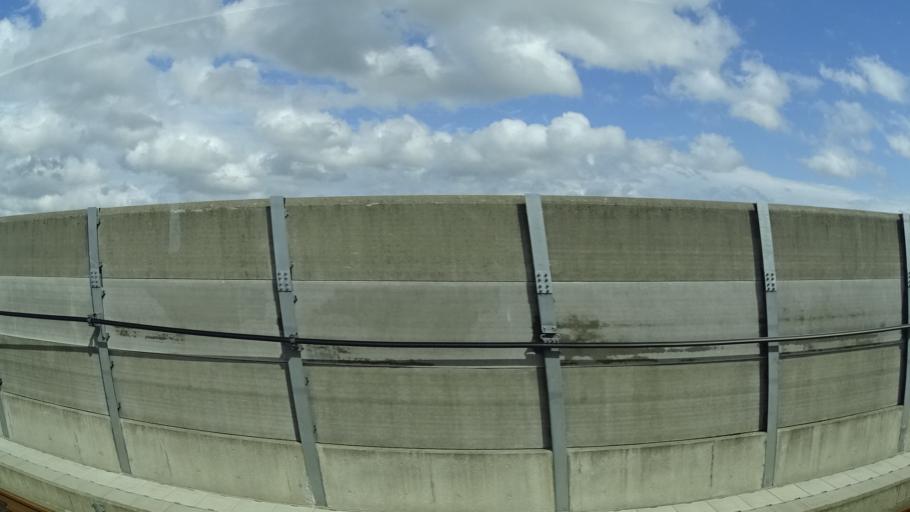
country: JP
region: Ishikawa
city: Kanazawa-shi
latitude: 36.5990
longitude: 136.6760
